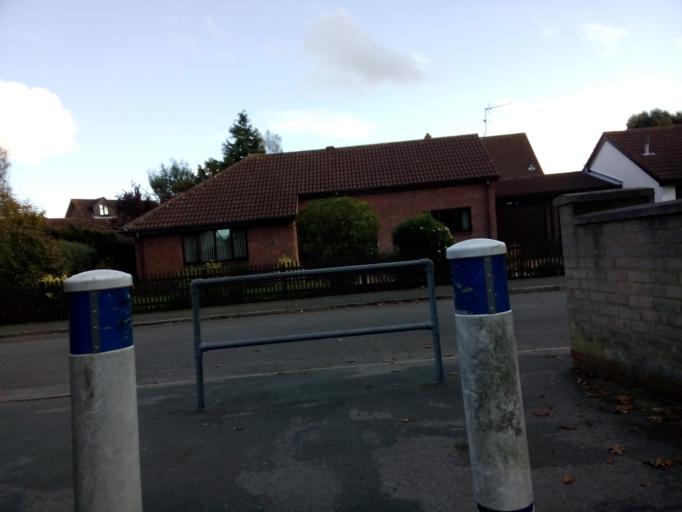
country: GB
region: England
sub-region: Suffolk
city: Kesgrave
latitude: 52.0616
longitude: 1.2661
